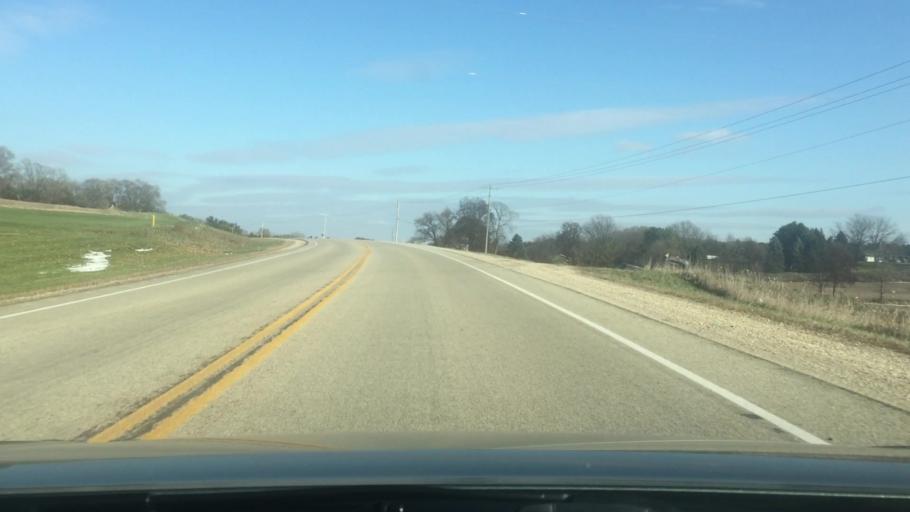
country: US
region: Wisconsin
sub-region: Jefferson County
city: Fort Atkinson
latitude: 42.9358
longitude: -88.7988
